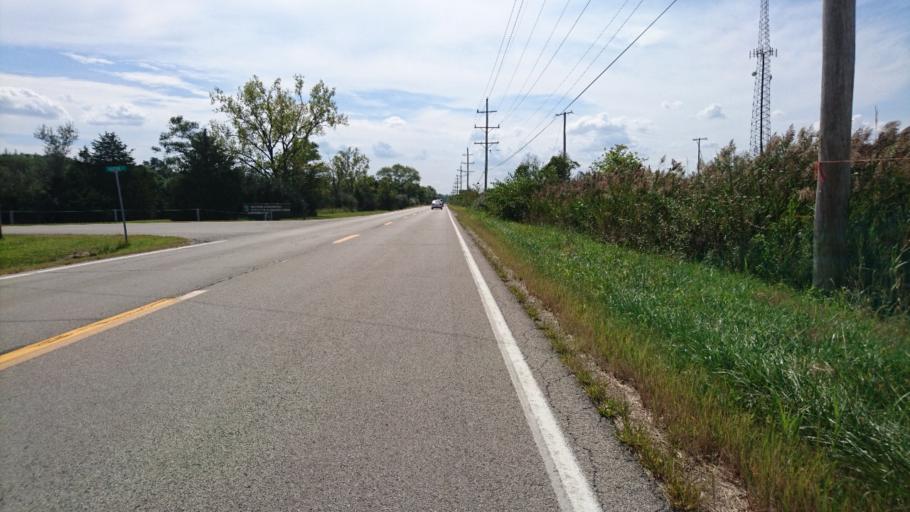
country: US
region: Illinois
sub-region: Grundy County
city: Central City
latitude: 41.2158
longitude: -88.2726
